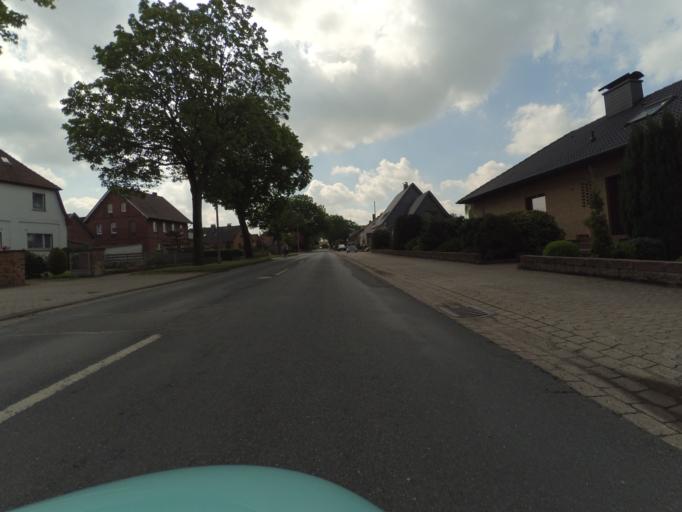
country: DE
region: Lower Saxony
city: Didderse
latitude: 52.3893
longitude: 10.3526
